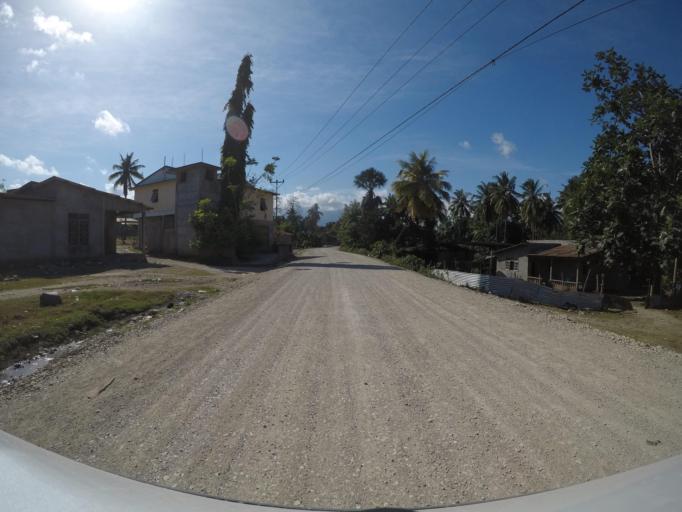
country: TL
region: Viqueque
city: Viqueque
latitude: -8.8477
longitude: 126.5125
